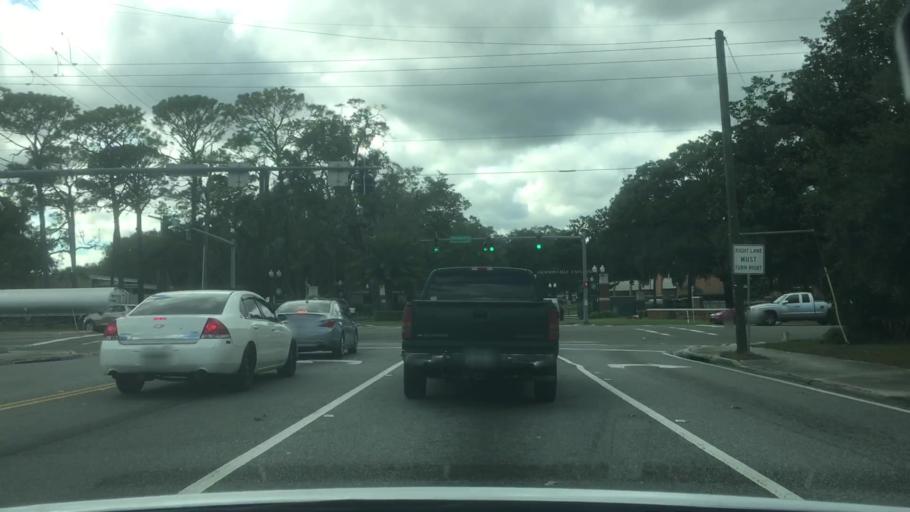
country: US
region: Florida
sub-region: Duval County
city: Jacksonville
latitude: 30.3517
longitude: -81.6021
